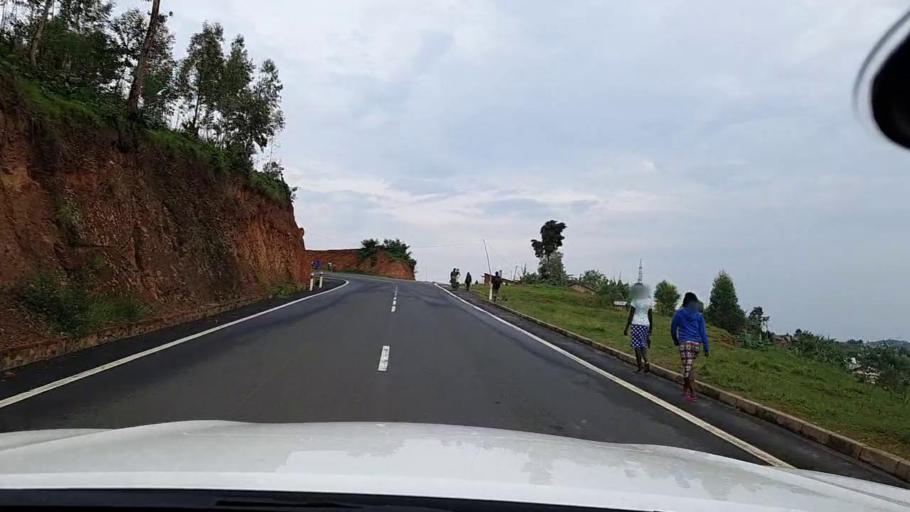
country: RW
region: Western Province
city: Kibuye
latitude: -2.1557
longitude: 29.2978
